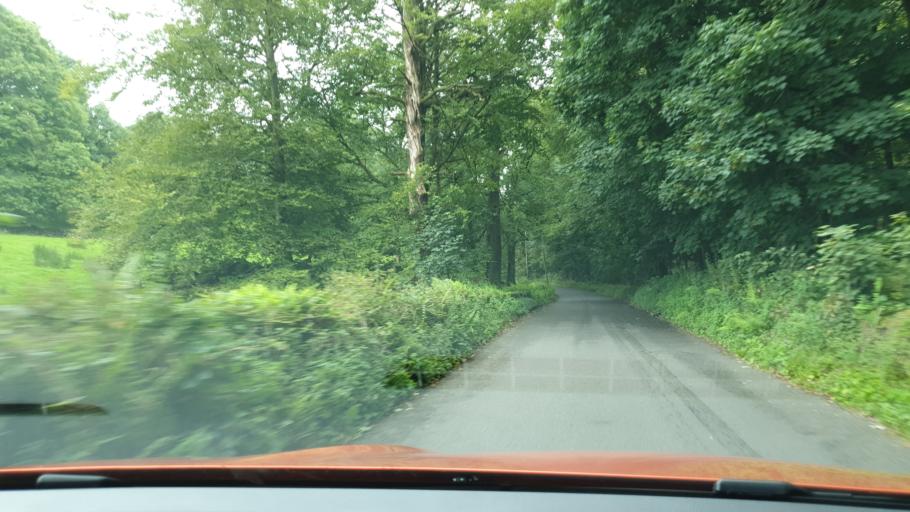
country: GB
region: England
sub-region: Cumbria
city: Grange-over-Sands
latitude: 54.2713
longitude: -2.9866
